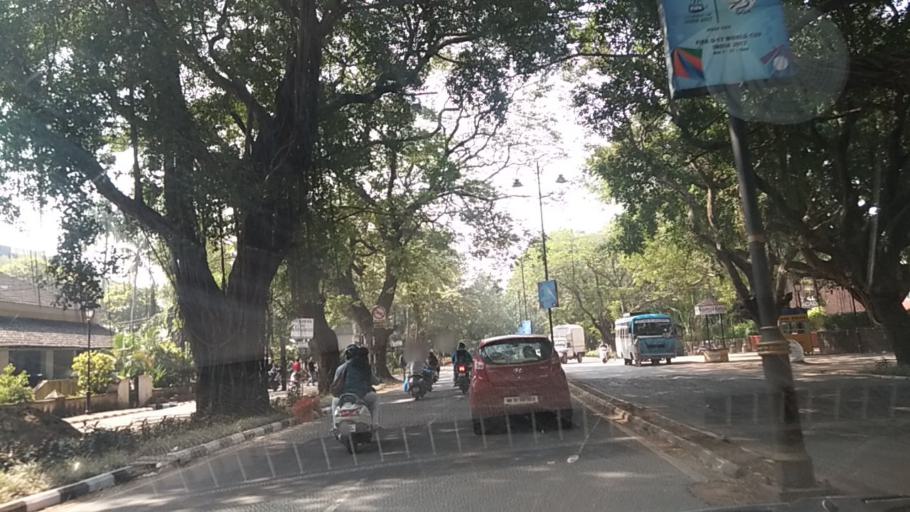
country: IN
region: Goa
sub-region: North Goa
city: Panaji
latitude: 15.4945
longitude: 73.8185
